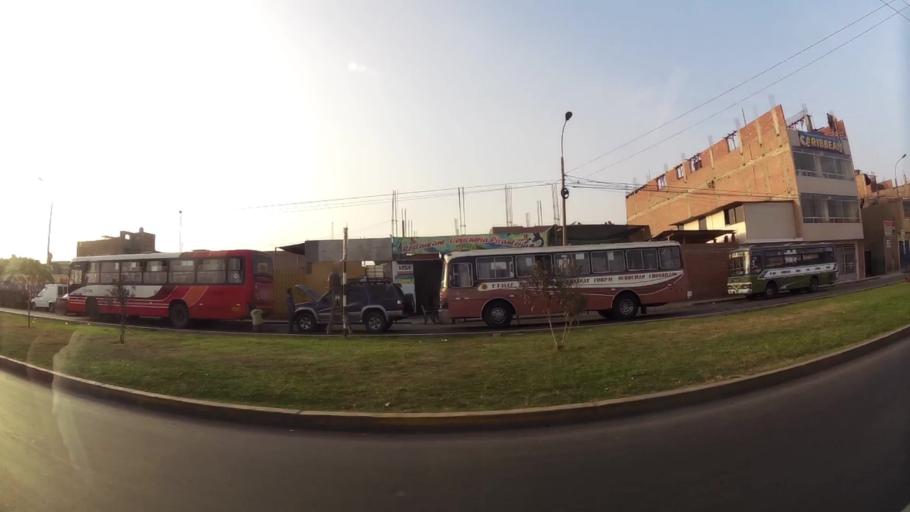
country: PE
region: Lima
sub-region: Lima
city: Independencia
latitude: -11.9896
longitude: -77.1005
